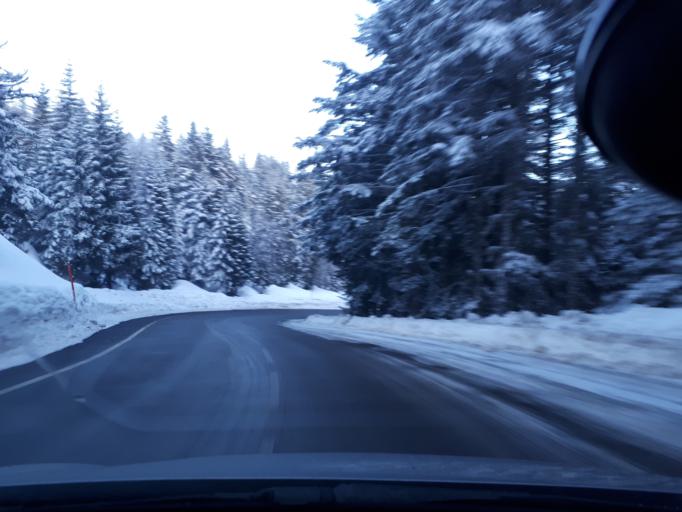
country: FR
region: Rhone-Alpes
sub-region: Departement de l'Isere
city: Vaulnaveys-le-Bas
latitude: 45.0985
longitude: 5.8676
